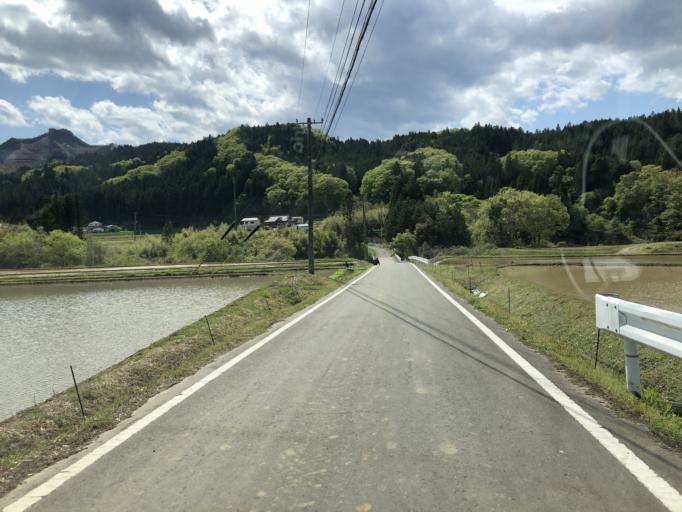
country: JP
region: Fukushima
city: Ishikawa
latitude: 37.0011
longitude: 140.3283
